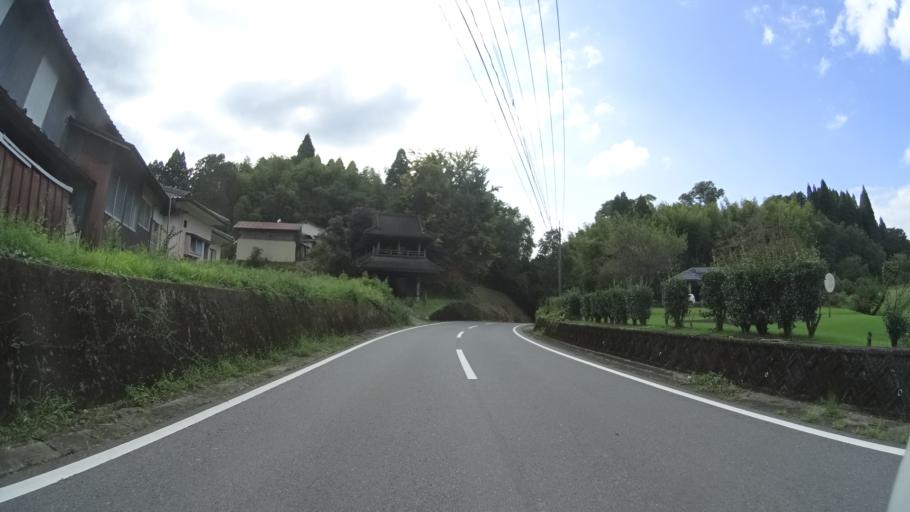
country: JP
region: Kumamoto
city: Aso
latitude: 32.7093
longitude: 131.1363
